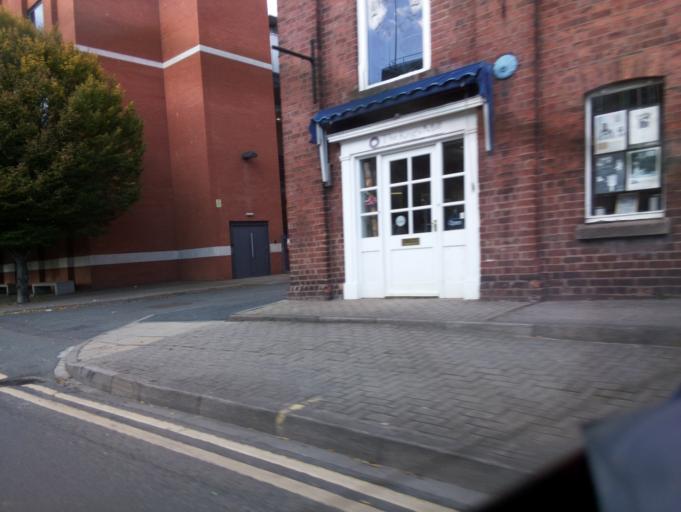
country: GB
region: England
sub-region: Herefordshire
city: Hereford
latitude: 52.0572
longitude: -2.7113
